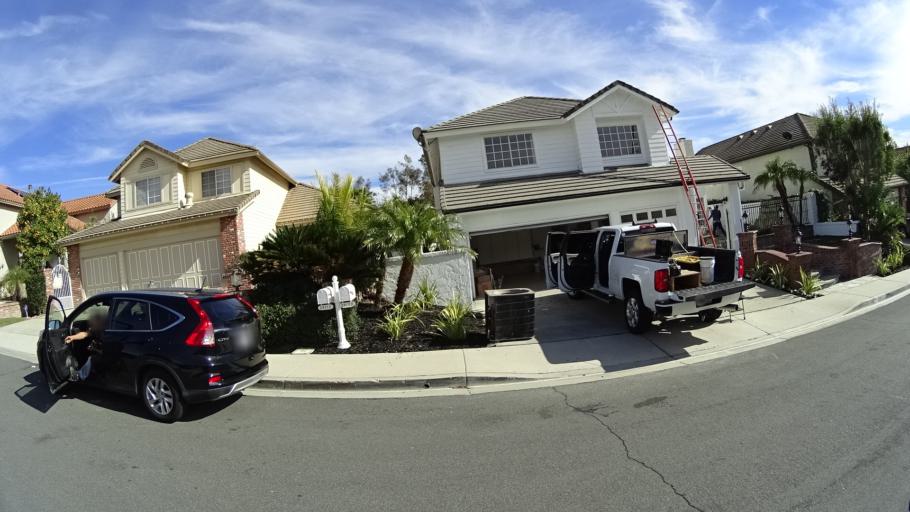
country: US
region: California
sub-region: Orange County
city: Portola Hills
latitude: 33.6806
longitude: -117.6229
